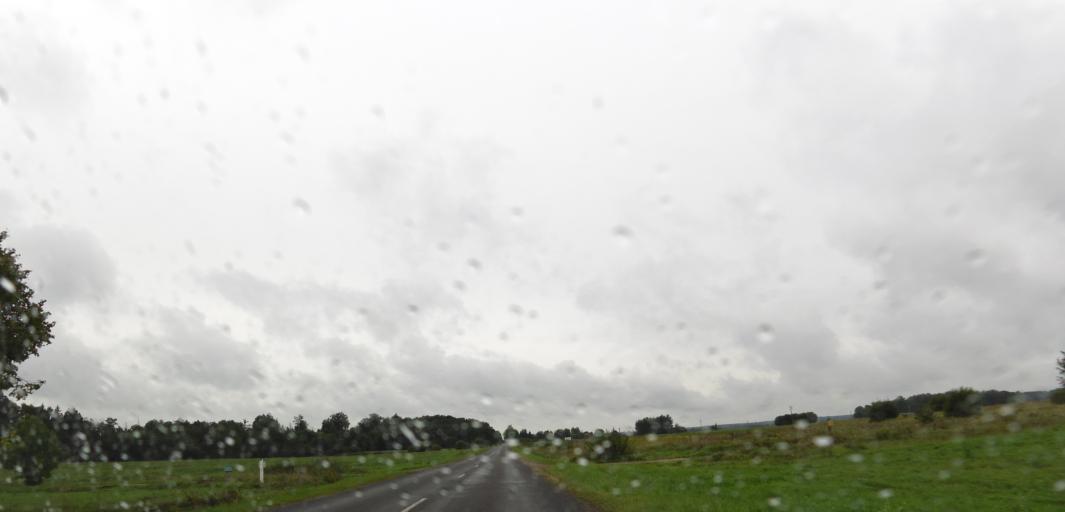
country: LT
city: Sirvintos
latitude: 55.0737
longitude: 24.9682
